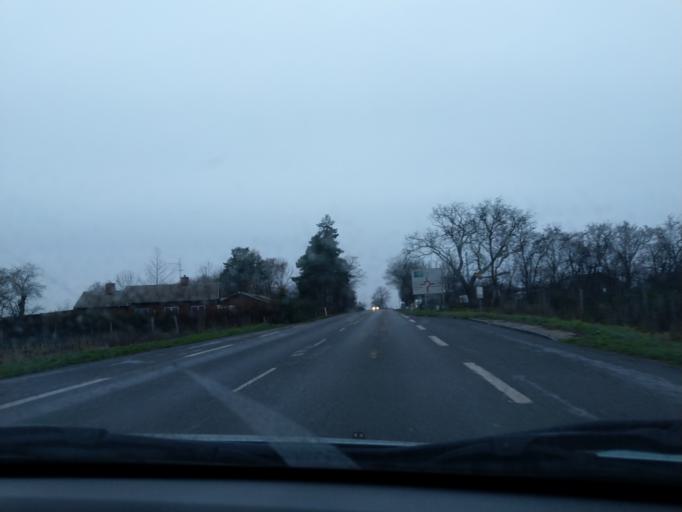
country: DK
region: Zealand
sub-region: Vordingborg Kommune
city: Orslev
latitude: 55.1204
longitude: 11.9727
